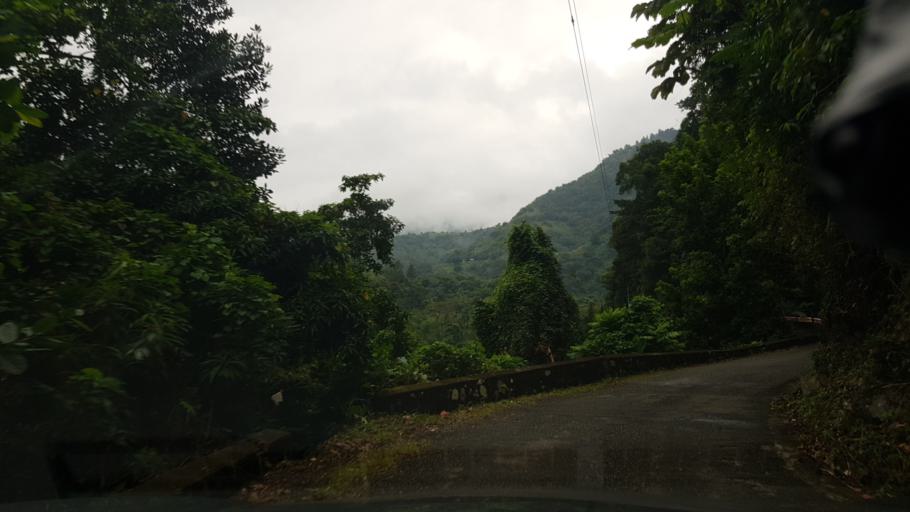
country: JM
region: Saint Andrew
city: Stony Hill
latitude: 18.1207
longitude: -76.7157
